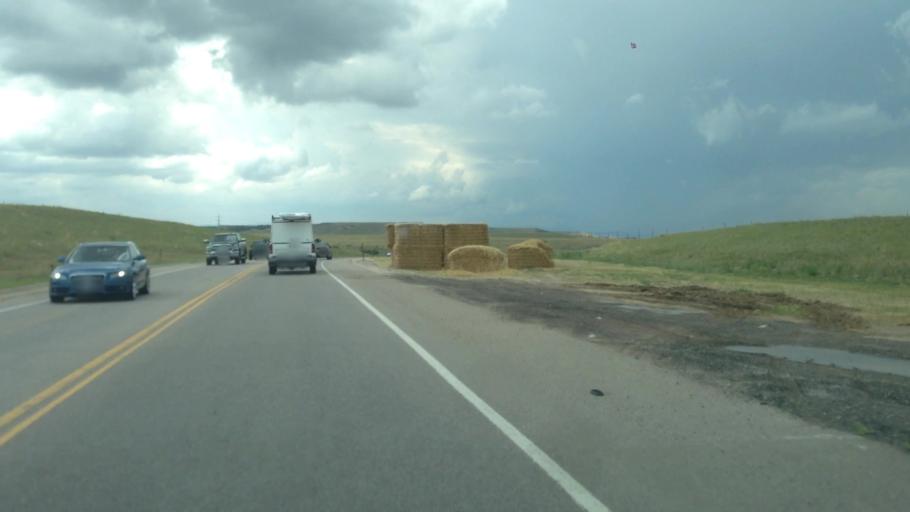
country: US
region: Colorado
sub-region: Douglas County
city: Stonegate
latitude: 39.5189
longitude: -104.8344
